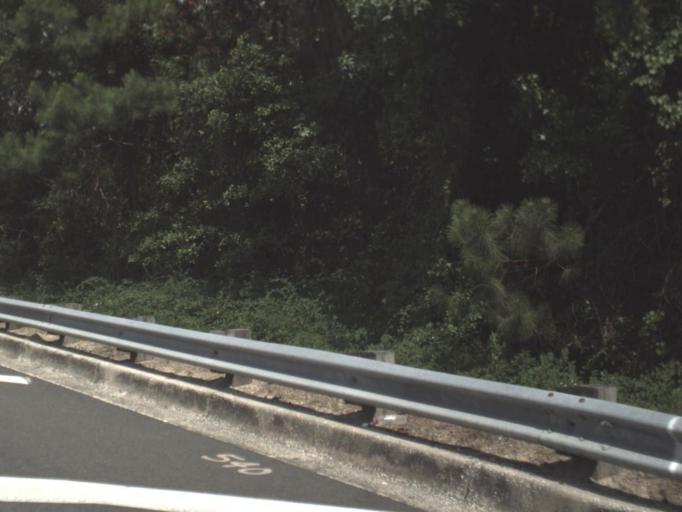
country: US
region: Georgia
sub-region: Echols County
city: Statenville
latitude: 30.5937
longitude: -83.1210
